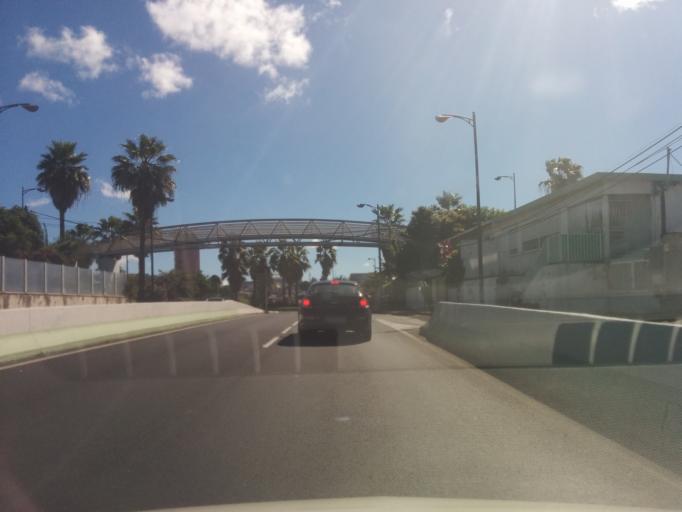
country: MQ
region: Martinique
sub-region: Martinique
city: Fort-de-France
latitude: 14.6057
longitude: -61.0913
